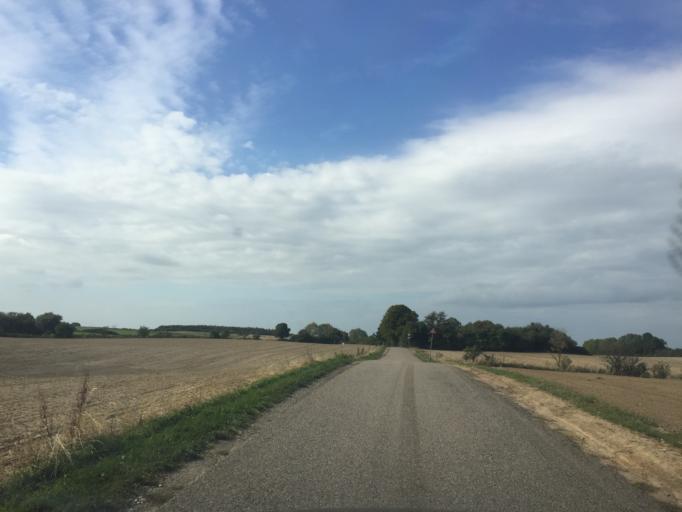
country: DK
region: Zealand
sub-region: Guldborgsund Kommune
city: Stubbekobing
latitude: 54.9264
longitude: 12.0237
